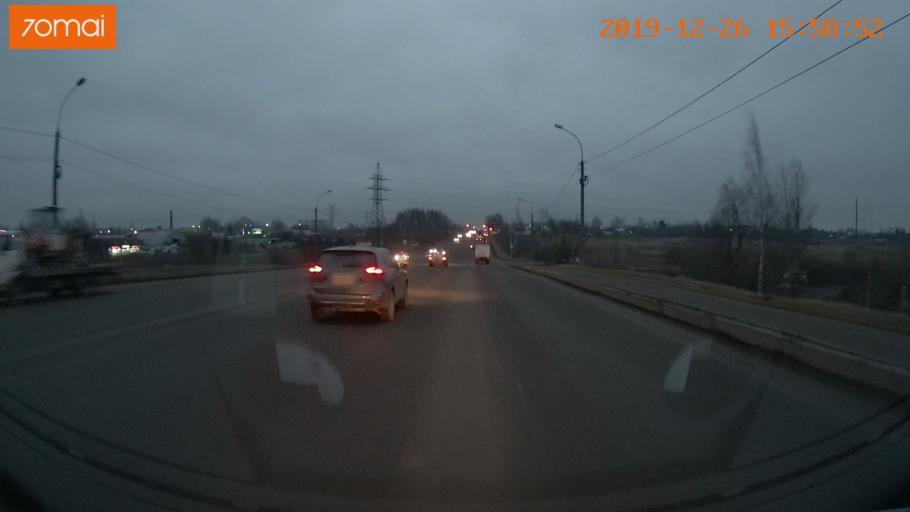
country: RU
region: Jaroslavl
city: Rybinsk
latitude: 58.0358
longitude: 38.7995
